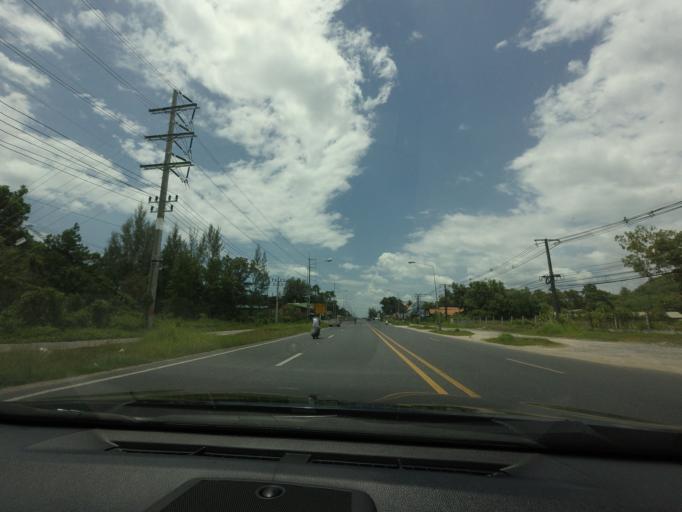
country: TH
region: Phangnga
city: Ban Khao Lak
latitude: 8.6550
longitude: 98.2535
